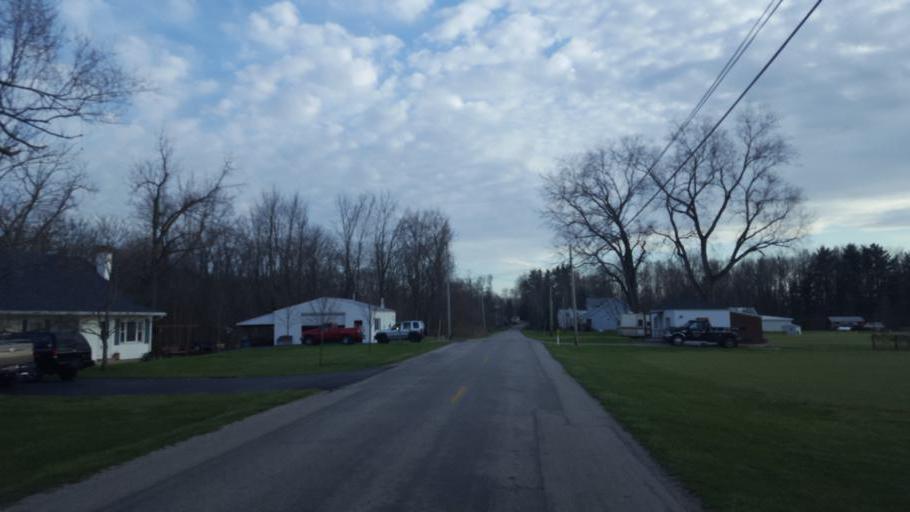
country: US
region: Ohio
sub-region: Morrow County
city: Cardington
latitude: 40.6448
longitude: -82.9655
